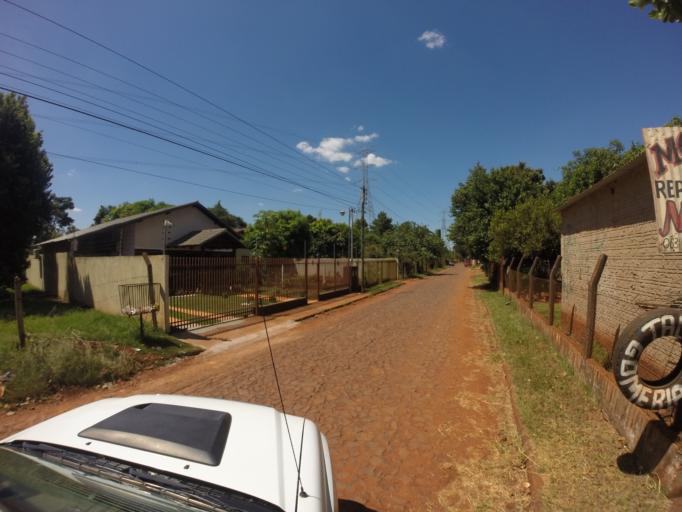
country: PY
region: Alto Parana
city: Ciudad del Este
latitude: -25.4298
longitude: -54.6427
